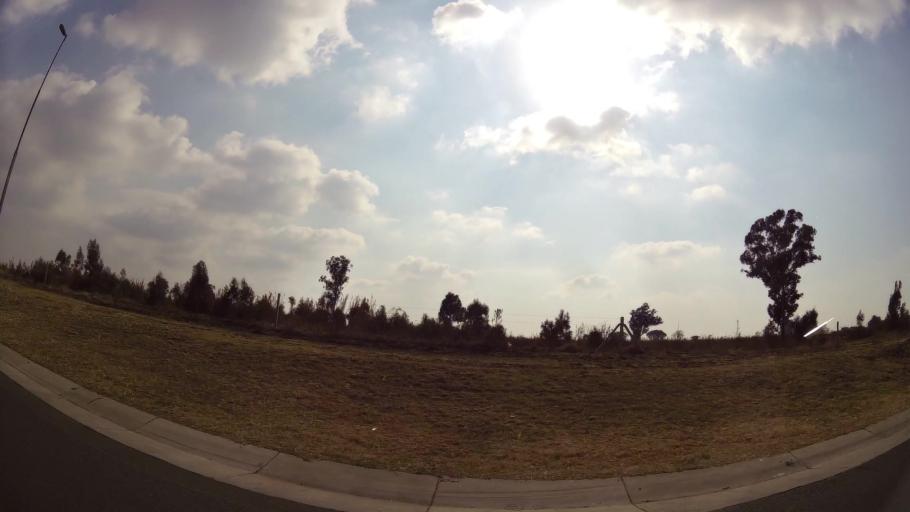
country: ZA
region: Gauteng
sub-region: Ekurhuleni Metropolitan Municipality
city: Benoni
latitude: -26.1673
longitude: 28.3870
